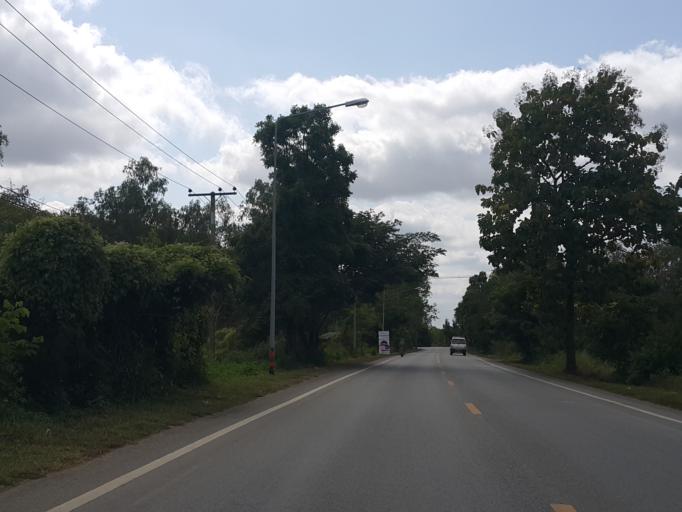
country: TH
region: Lamphun
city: Ban Thi
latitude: 18.6074
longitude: 99.0887
